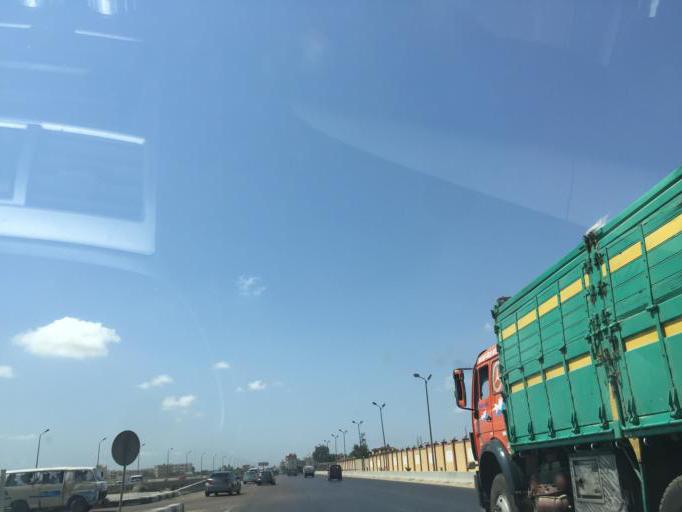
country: EG
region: Alexandria
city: Alexandria
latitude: 30.9967
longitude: 29.8089
